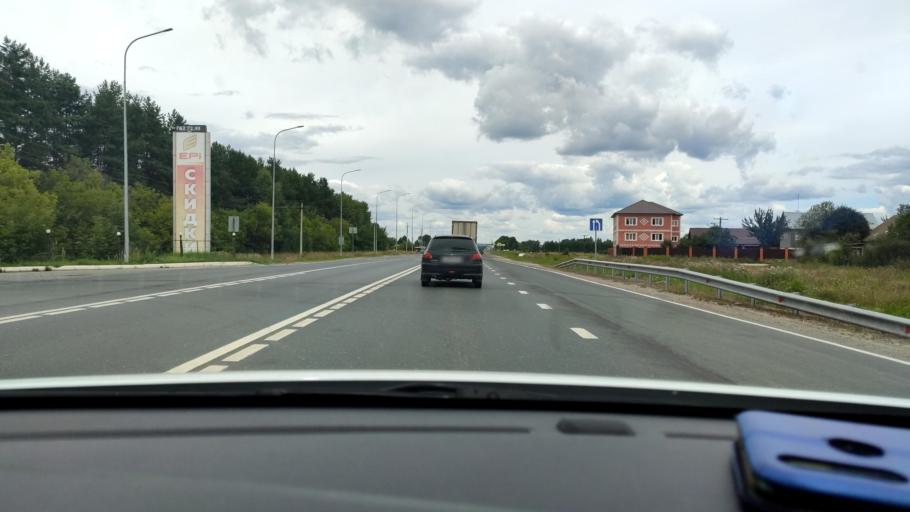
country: RU
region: Mariy-El
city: Pomary
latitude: 55.9622
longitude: 48.3655
